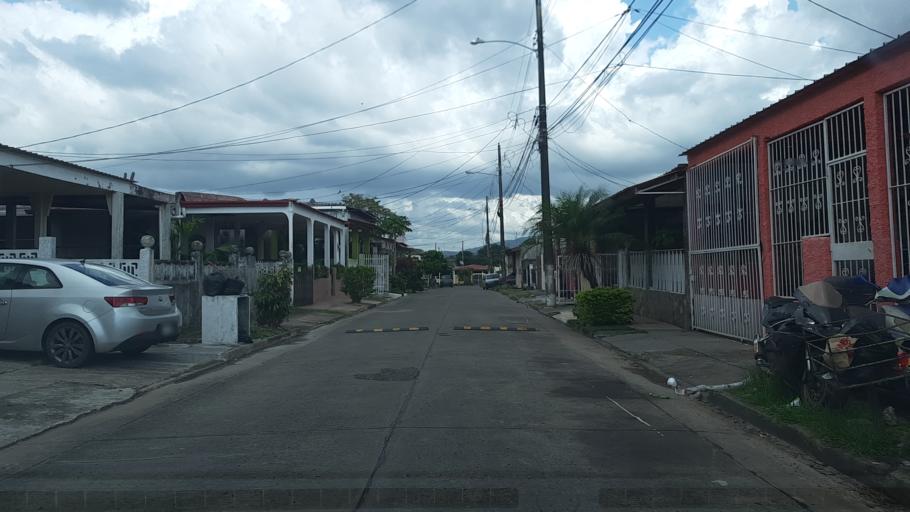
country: PA
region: Panama
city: Tocumen
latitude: 9.0557
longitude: -79.4098
